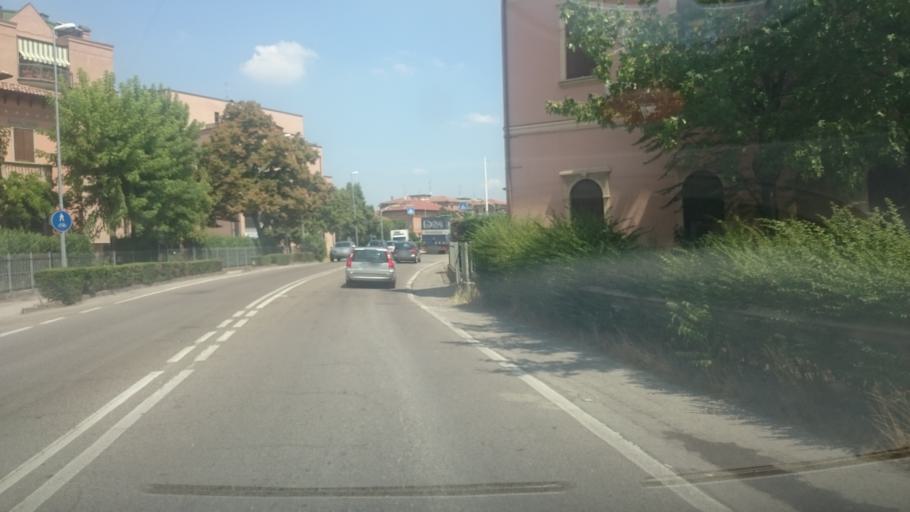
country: IT
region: Emilia-Romagna
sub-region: Provincia di Reggio Emilia
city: Rubiera
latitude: 44.6542
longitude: 10.7794
